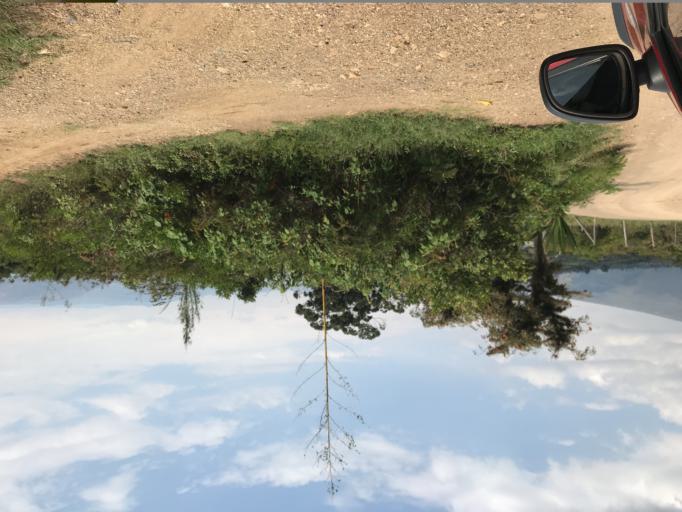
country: CO
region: Boyaca
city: Villa de Leiva
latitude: 5.6478
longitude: -73.5630
